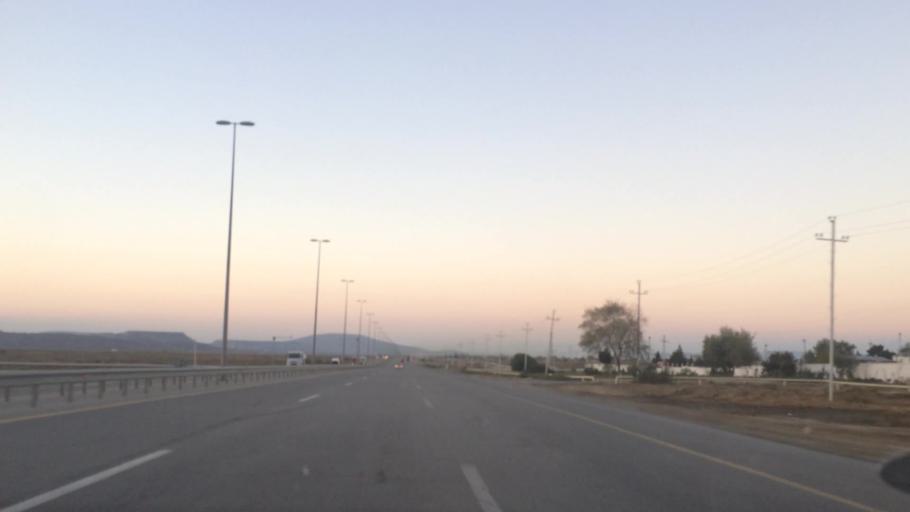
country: AZ
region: Baki
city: Qobustan
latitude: 40.0006
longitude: 49.4289
